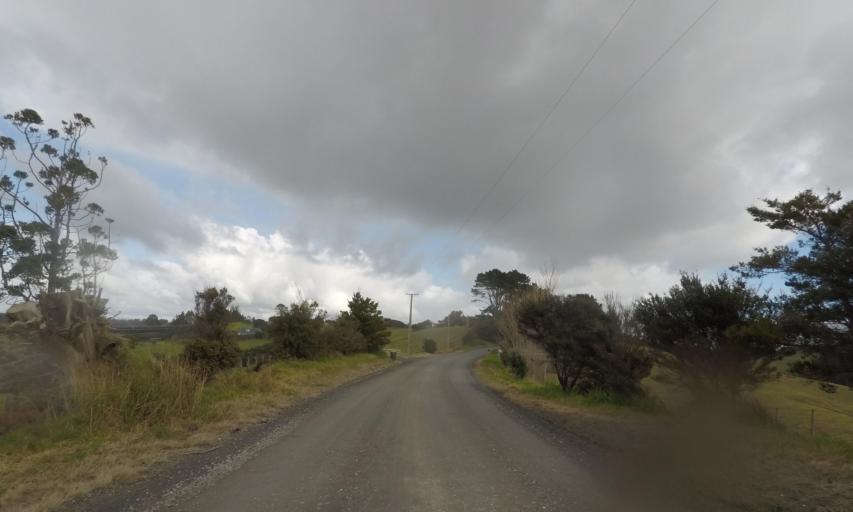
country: NZ
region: Auckland
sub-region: Auckland
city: Wellsford
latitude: -36.1723
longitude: 174.6004
